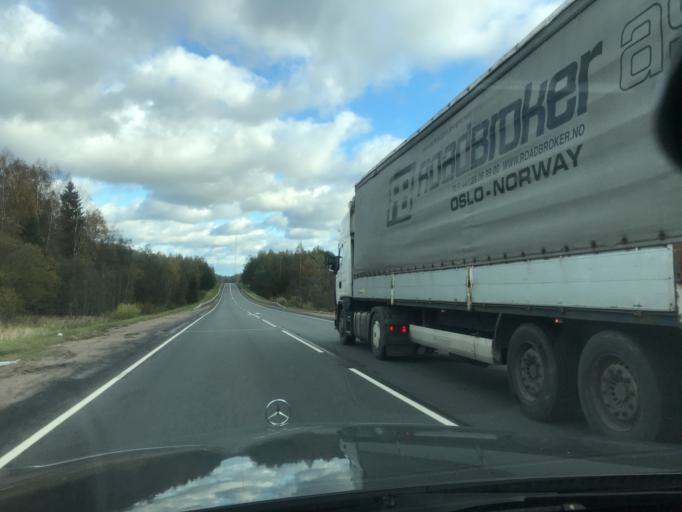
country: RU
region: Pskov
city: Novosokol'niki
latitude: 56.3431
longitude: 29.9513
